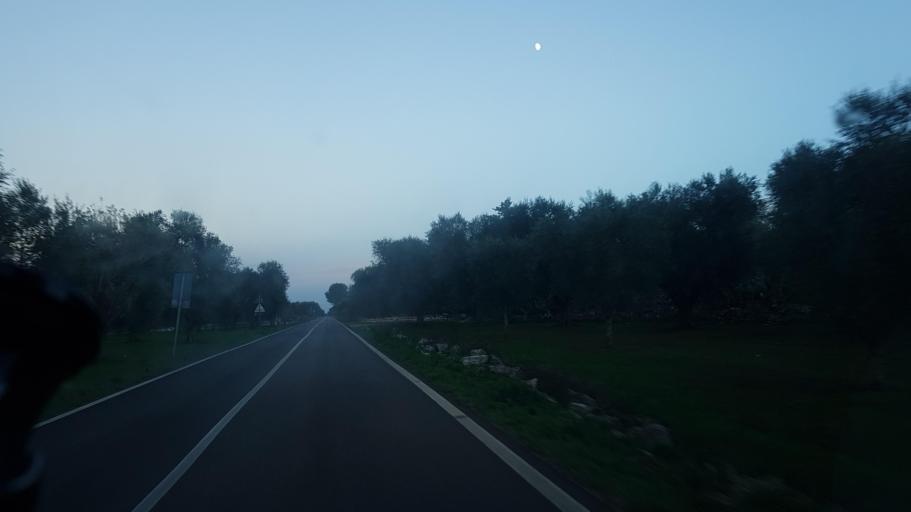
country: IT
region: Apulia
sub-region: Provincia di Brindisi
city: Latiano
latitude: 40.5696
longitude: 17.6658
